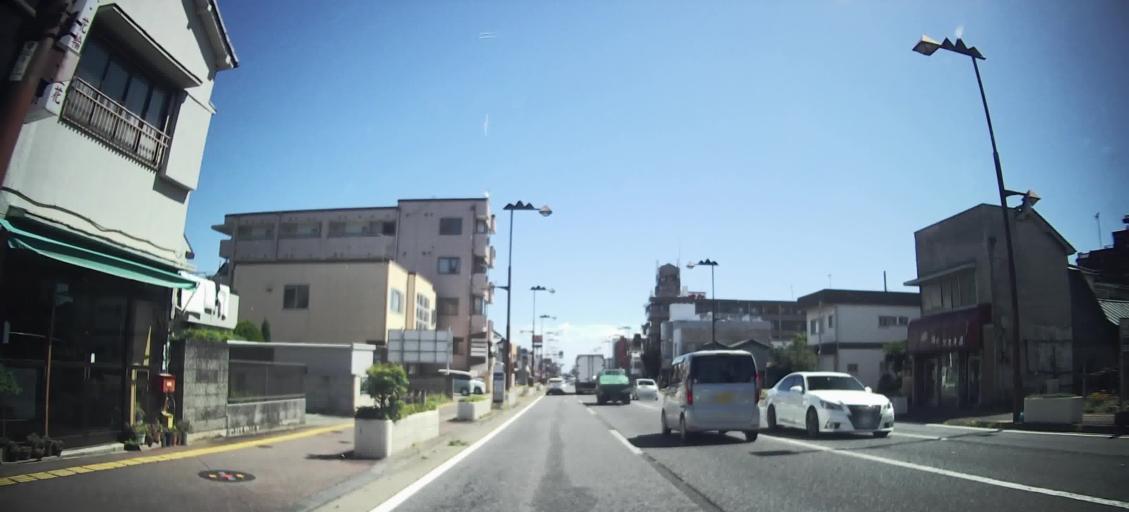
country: JP
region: Gunma
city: Maebashi-shi
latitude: 36.3855
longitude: 139.0783
